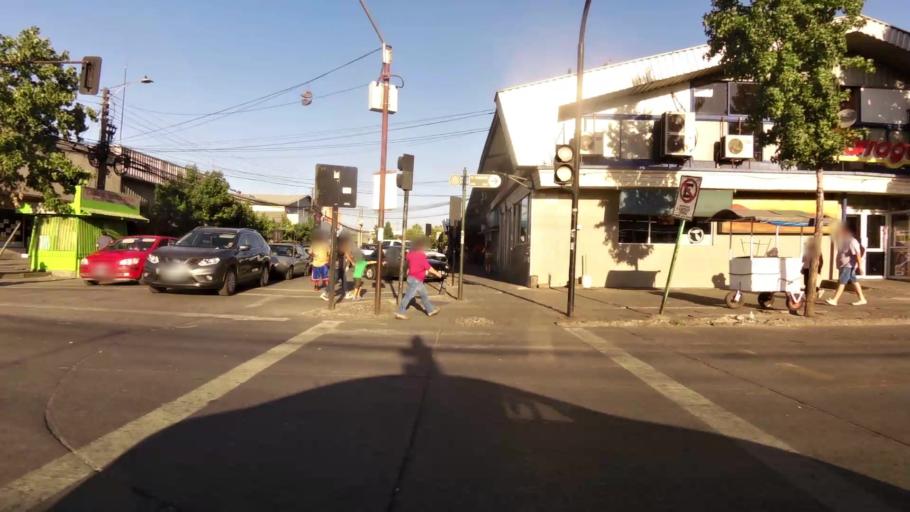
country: CL
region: Maule
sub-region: Provincia de Talca
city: Talca
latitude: -35.4298
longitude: -71.6481
